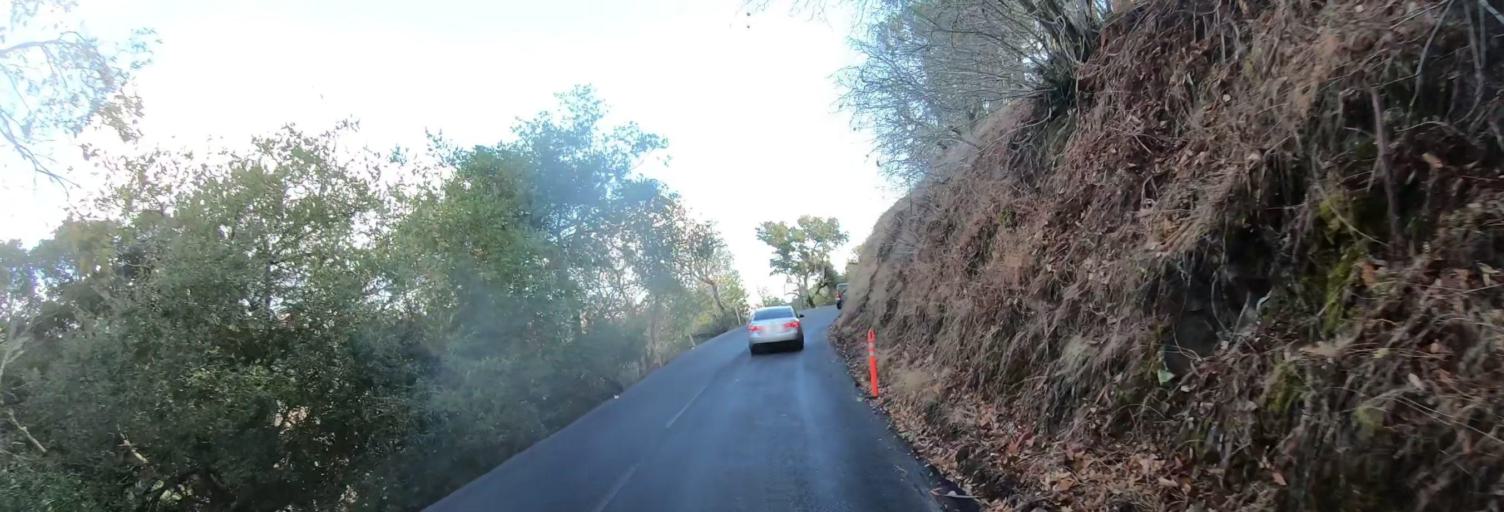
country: US
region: California
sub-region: Santa Clara County
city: East Foothills
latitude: 37.3629
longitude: -121.7555
